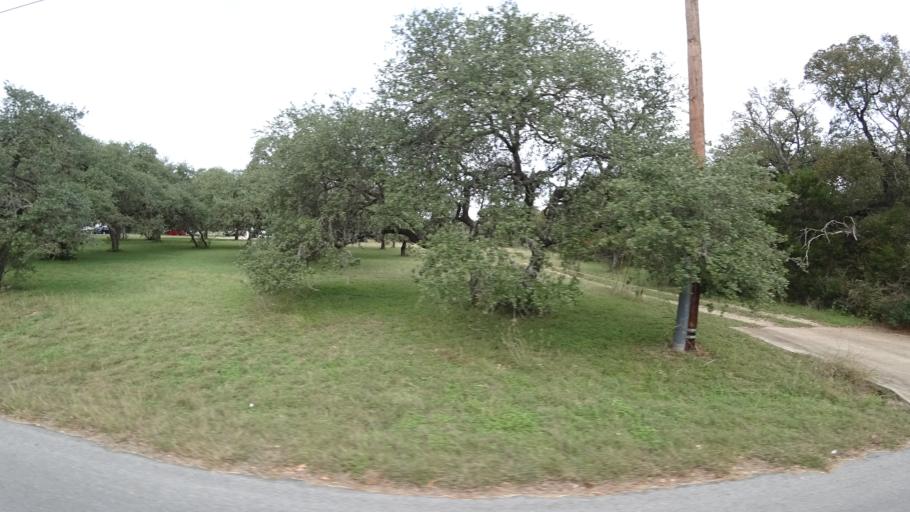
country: US
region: Texas
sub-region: Travis County
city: Shady Hollow
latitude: 30.1454
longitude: -97.8784
